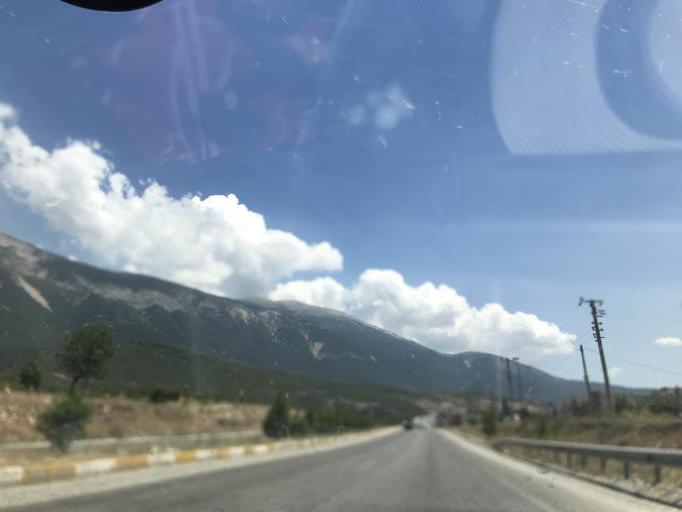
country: TR
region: Denizli
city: Honaz
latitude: 37.6978
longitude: 29.2021
